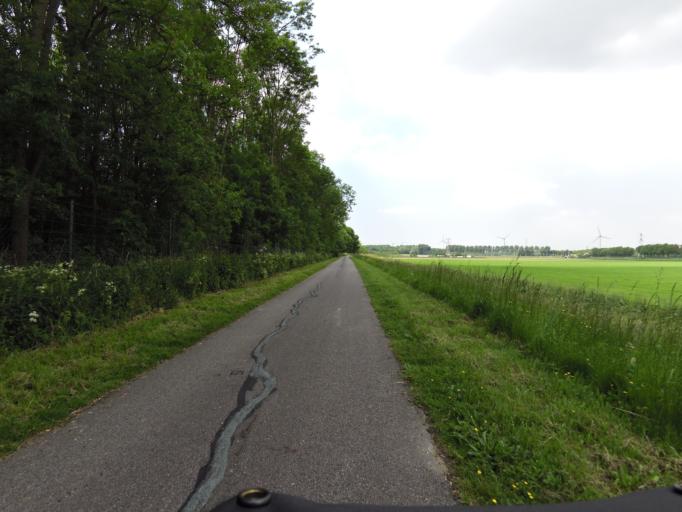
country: NL
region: South Holland
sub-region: Gemeente Maassluis
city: Maassluis
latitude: 51.8509
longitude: 4.2499
